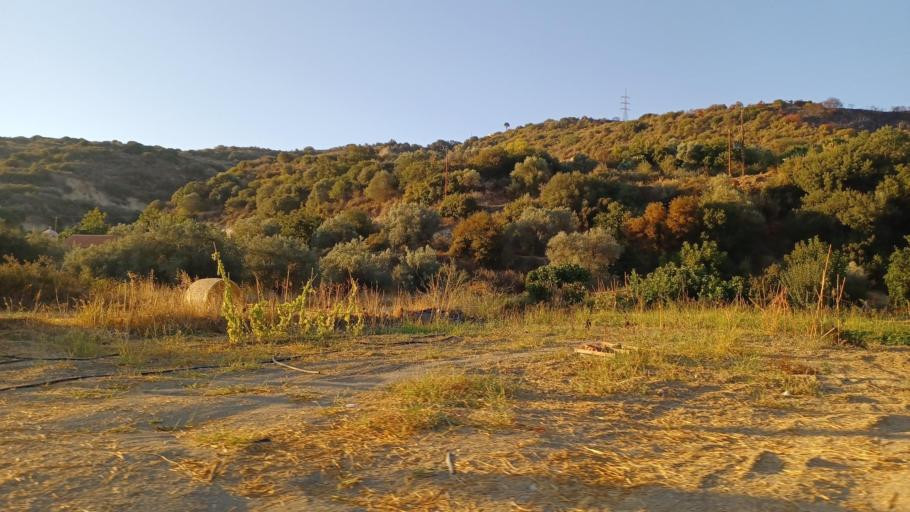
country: CY
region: Pafos
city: Polis
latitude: 34.9779
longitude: 32.4608
